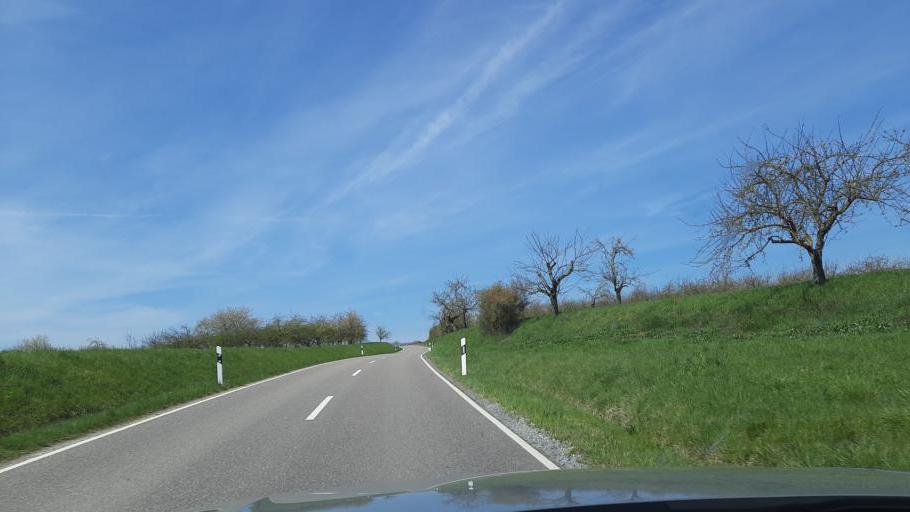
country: DE
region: Baden-Wuerttemberg
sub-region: Regierungsbezirk Stuttgart
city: Neuenstadt am Kocher
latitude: 49.2198
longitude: 9.3755
